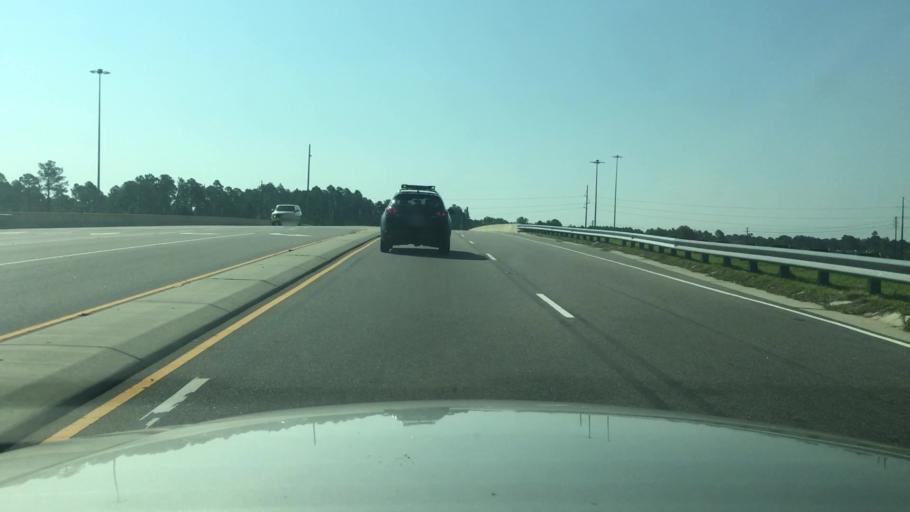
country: US
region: North Carolina
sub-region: Cumberland County
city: Spring Lake
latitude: 35.1406
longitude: -78.9073
